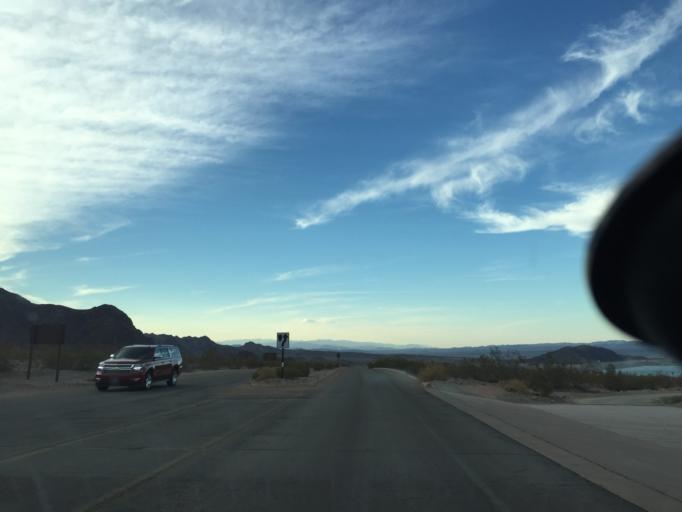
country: US
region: Nevada
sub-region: Clark County
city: Boulder City
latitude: 36.0236
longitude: -114.7975
